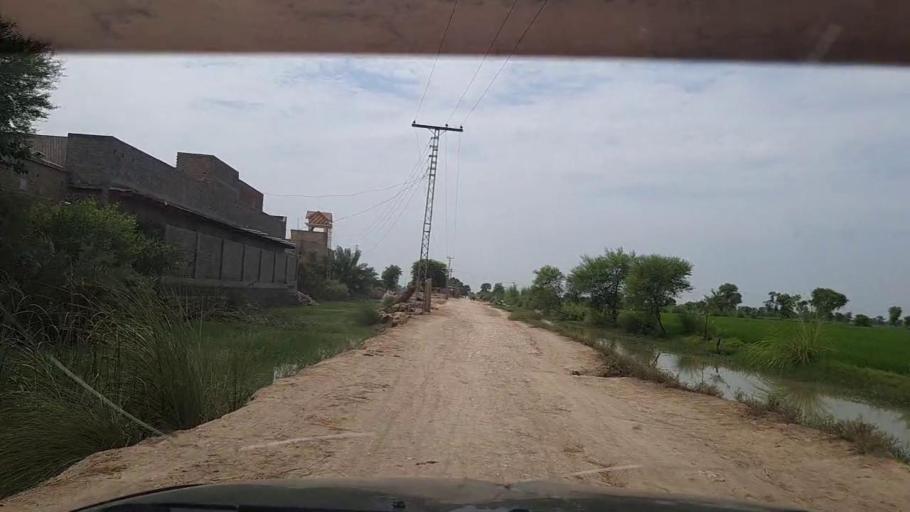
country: PK
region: Sindh
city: Thul
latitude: 28.2438
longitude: 68.7317
